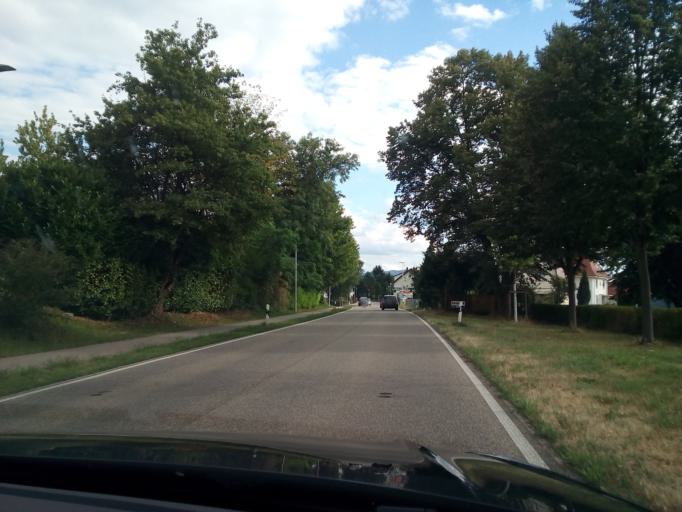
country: DE
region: Baden-Wuerttemberg
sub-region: Freiburg Region
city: Appenweier
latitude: 48.5441
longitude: 7.9777
